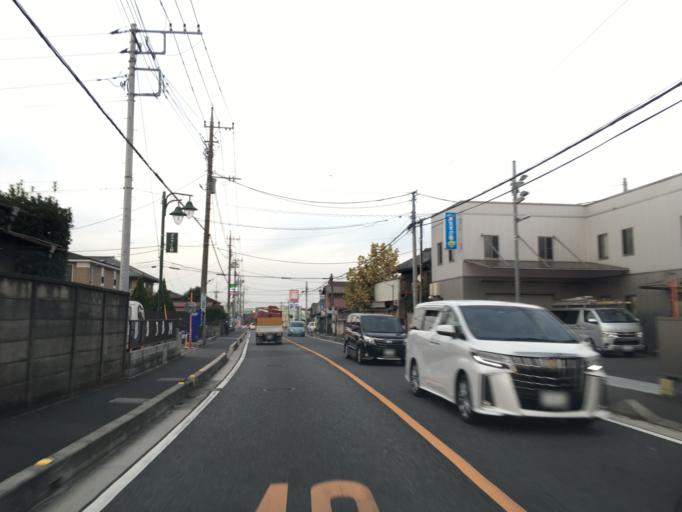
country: JP
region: Saitama
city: Sayama
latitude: 35.8470
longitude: 139.3838
